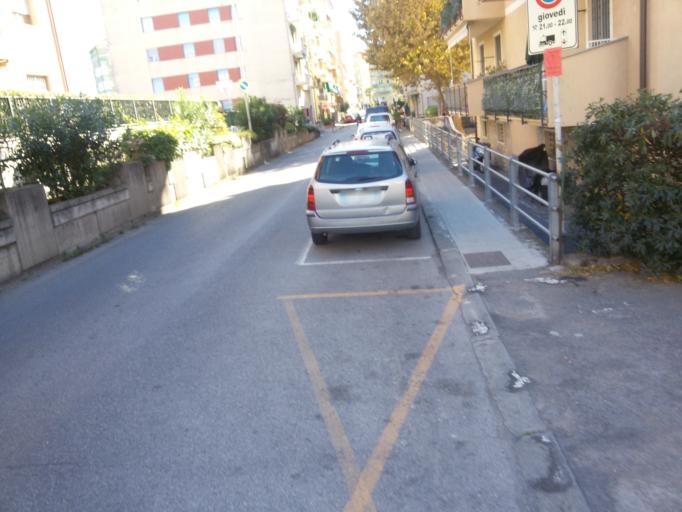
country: IT
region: Liguria
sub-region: Provincia di Genova
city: Chiavari
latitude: 44.3234
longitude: 9.3213
